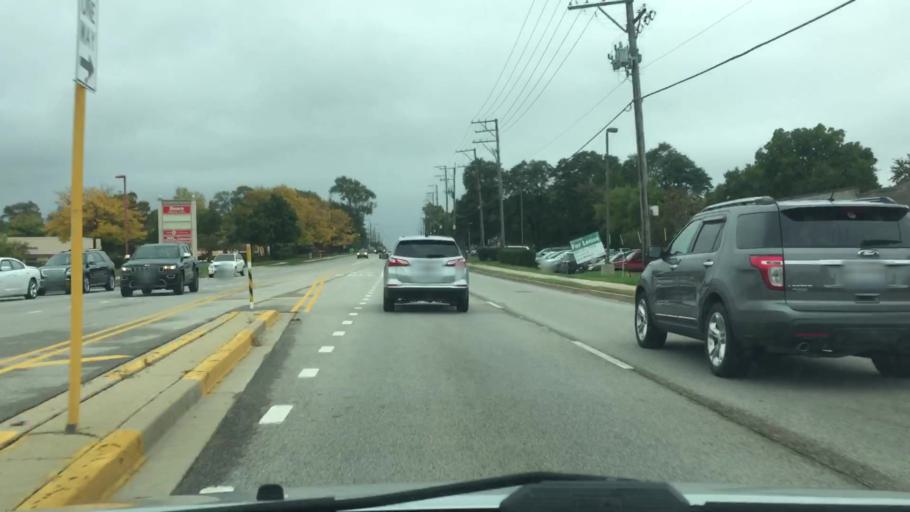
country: US
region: Illinois
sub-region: McHenry County
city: McHenry
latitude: 42.3529
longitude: -88.2674
